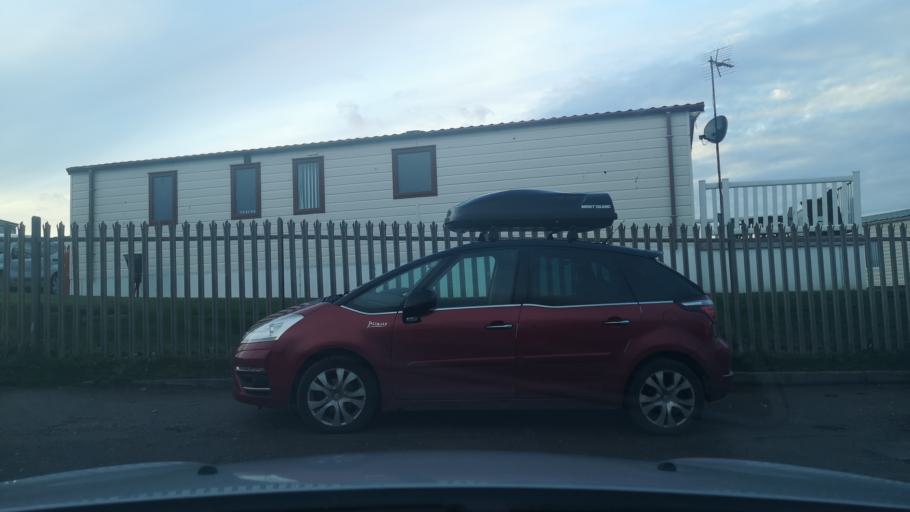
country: GB
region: England
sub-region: East Riding of Yorkshire
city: Hornsea
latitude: 53.9073
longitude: -0.1576
